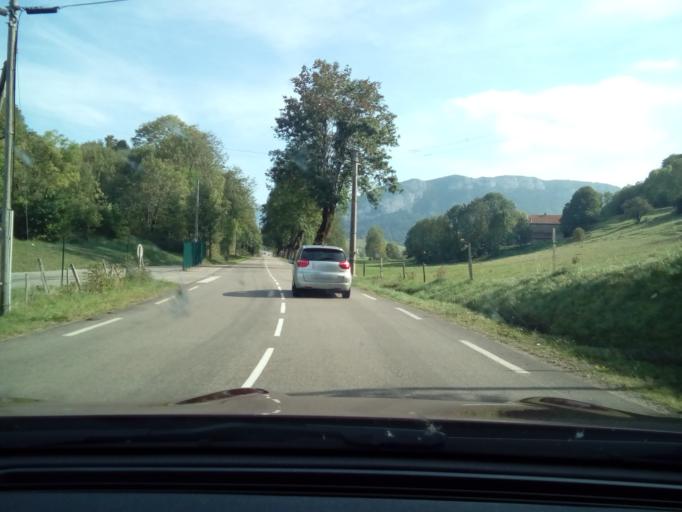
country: FR
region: Rhone-Alpes
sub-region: Departement de la Drome
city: Saint-Laurent-en-Royans
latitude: 44.9773
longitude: 5.3991
